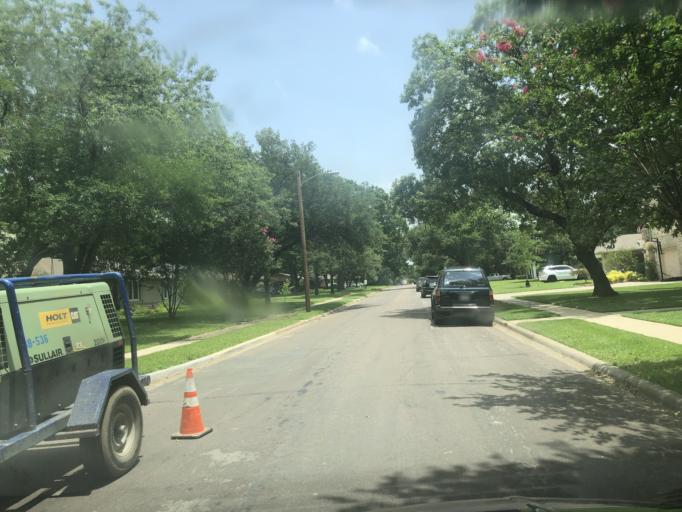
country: US
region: Texas
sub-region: Dallas County
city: University Park
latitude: 32.8699
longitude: -96.8420
